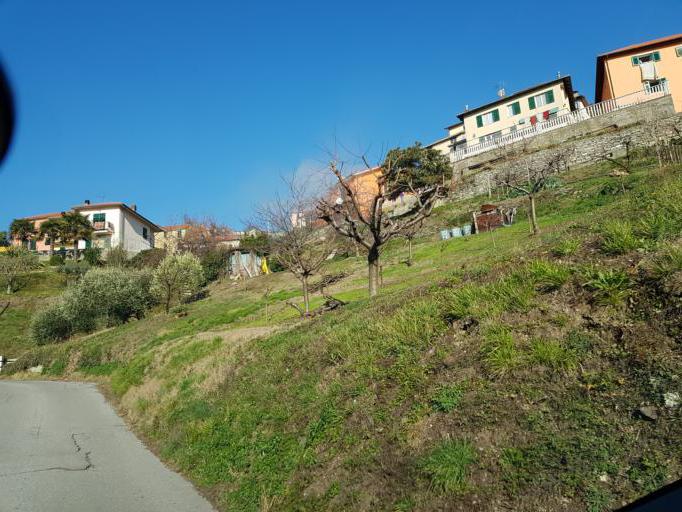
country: IT
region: Liguria
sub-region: Provincia di Genova
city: Campomorone
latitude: 44.4997
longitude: 8.8803
